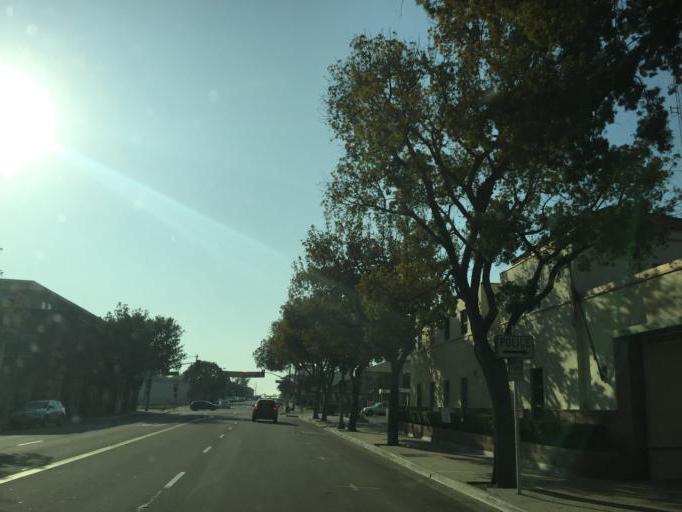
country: US
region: California
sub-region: Los Angeles County
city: South Pasadena
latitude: 34.1159
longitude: -118.1521
